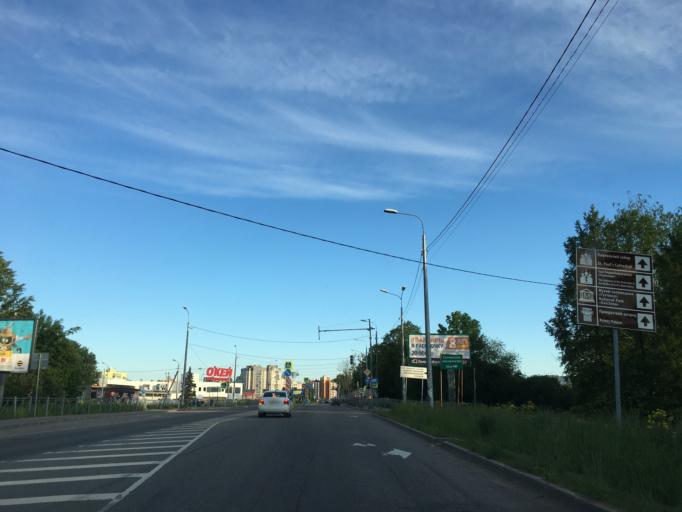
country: RU
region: Leningrad
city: Gatchina
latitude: 59.5860
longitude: 30.1361
